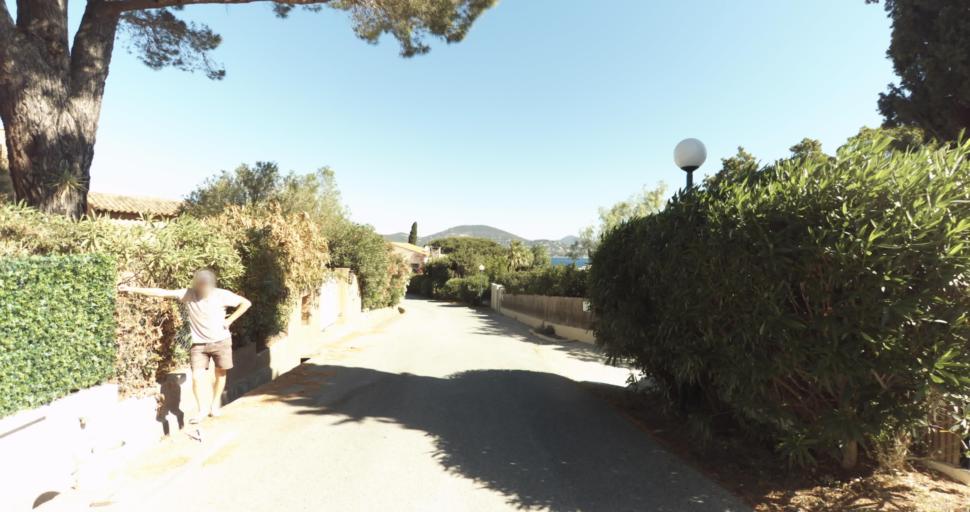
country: FR
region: Provence-Alpes-Cote d'Azur
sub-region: Departement du Var
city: Saint-Tropez
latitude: 43.2615
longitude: 6.6133
